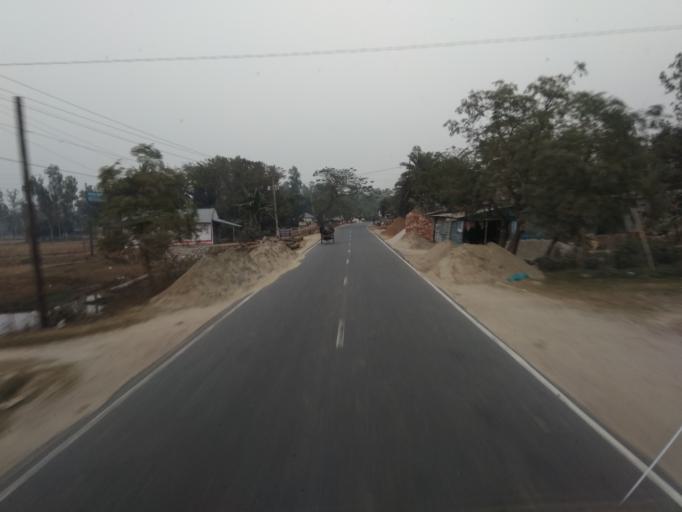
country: BD
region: Rajshahi
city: Bogra
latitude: 24.6490
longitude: 89.2569
